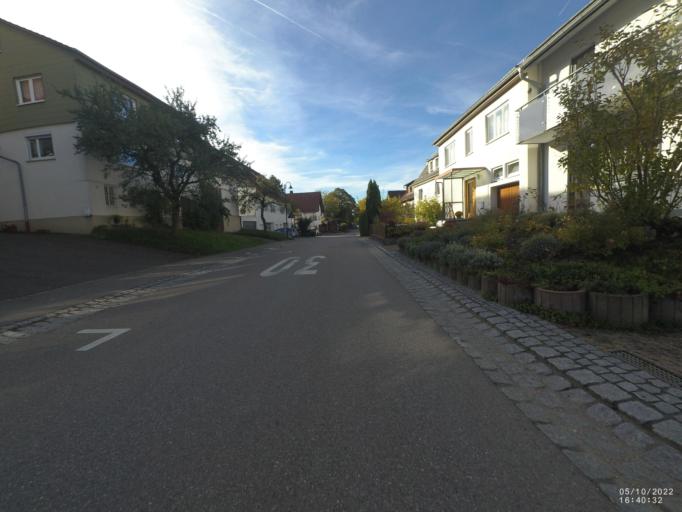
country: DE
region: Baden-Wuerttemberg
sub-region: Regierungsbezirk Stuttgart
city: Schlierbach
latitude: 48.6910
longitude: 9.5015
